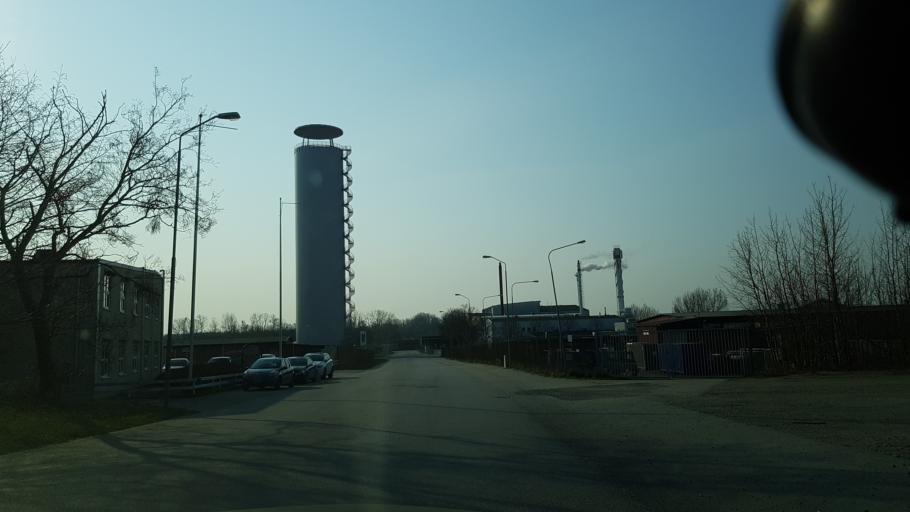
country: SE
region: Skane
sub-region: Ystads Kommun
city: Ystad
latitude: 55.4427
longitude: 13.8409
